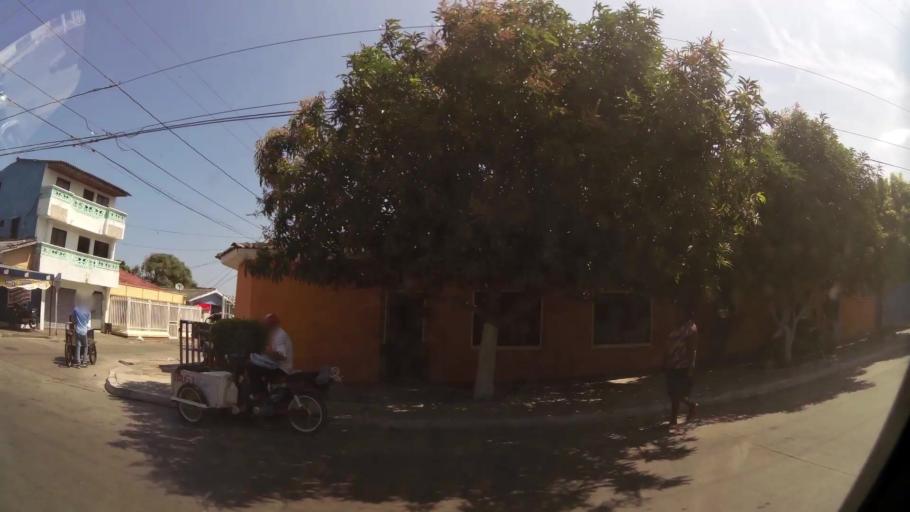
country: CO
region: Atlantico
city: Barranquilla
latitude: 10.9706
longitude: -74.8111
